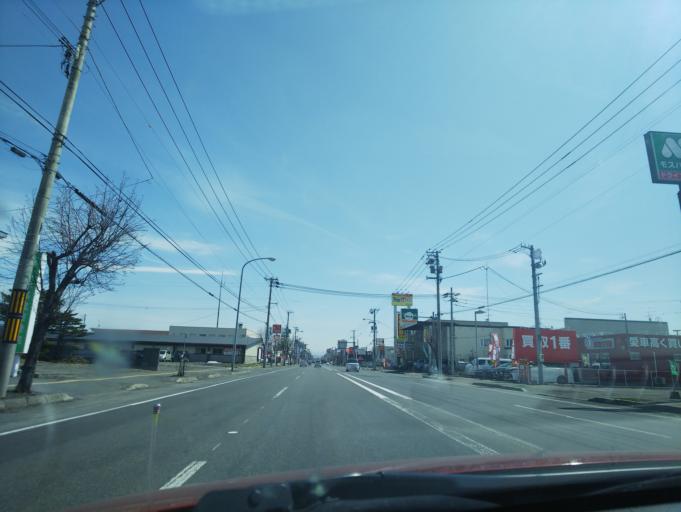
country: JP
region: Hokkaido
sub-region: Asahikawa-shi
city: Asahikawa
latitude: 43.7900
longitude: 142.4056
